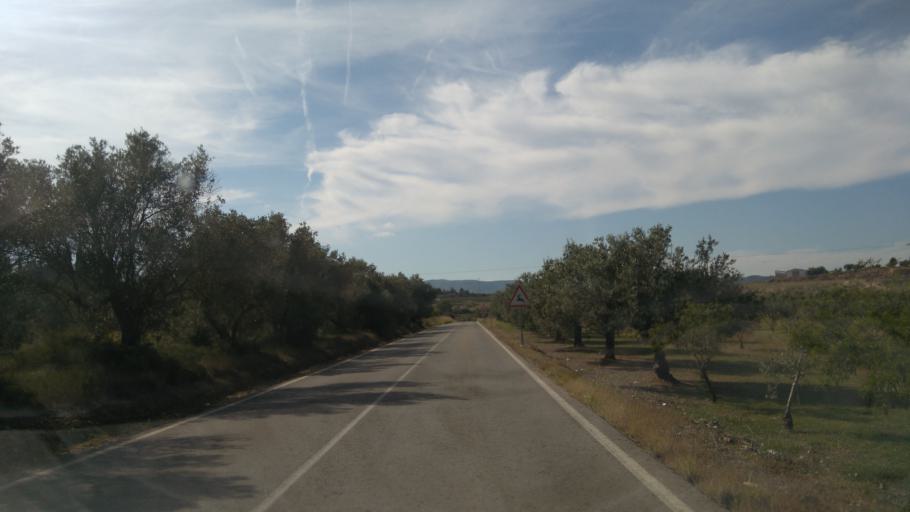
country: ES
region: Valencia
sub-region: Provincia de Valencia
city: Real de Montroi
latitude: 39.3303
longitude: -0.5980
